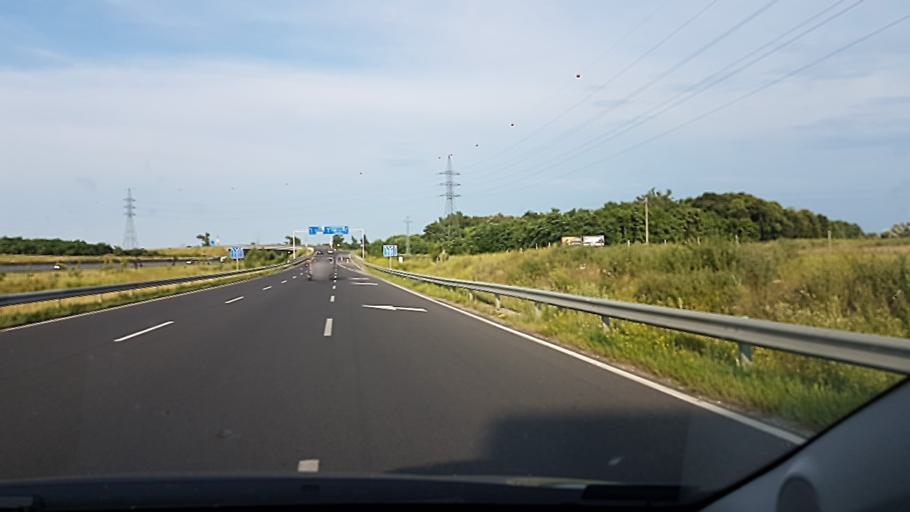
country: HU
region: Pest
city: Dunaharaszti
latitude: 47.3678
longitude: 19.1195
